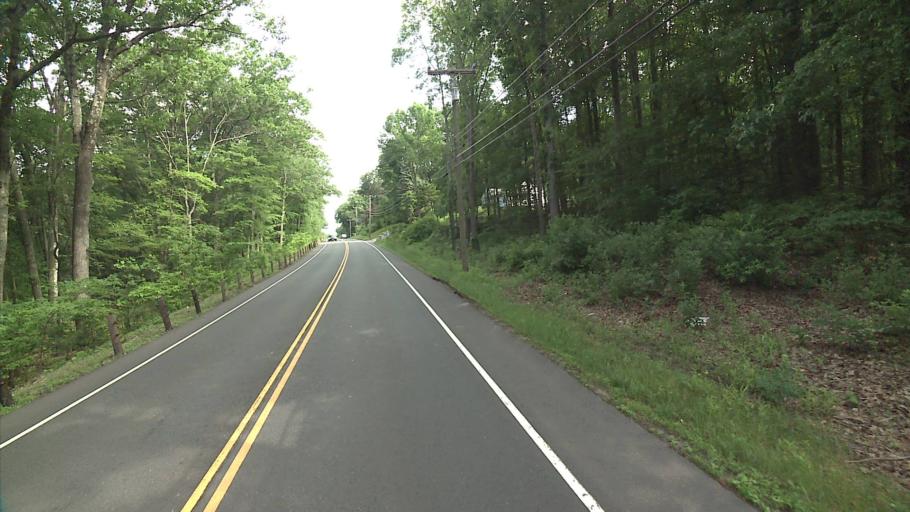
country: US
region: Connecticut
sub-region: Litchfield County
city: Oakville
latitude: 41.5603
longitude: -73.0941
